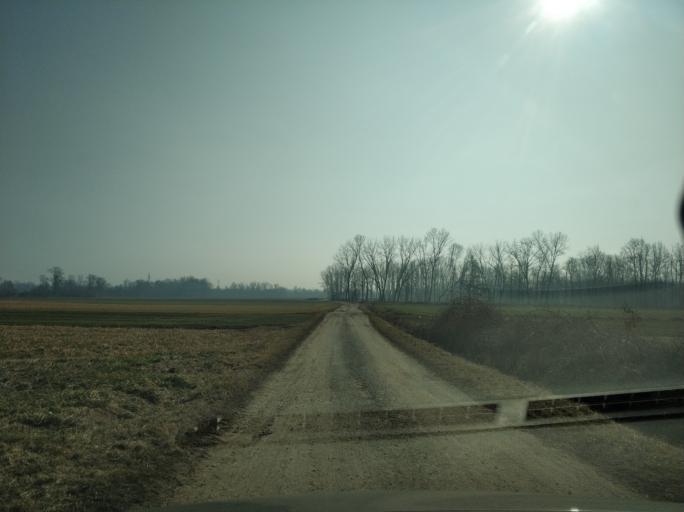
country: IT
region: Piedmont
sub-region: Provincia di Torino
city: Rivarossa
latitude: 45.2520
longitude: 7.7289
